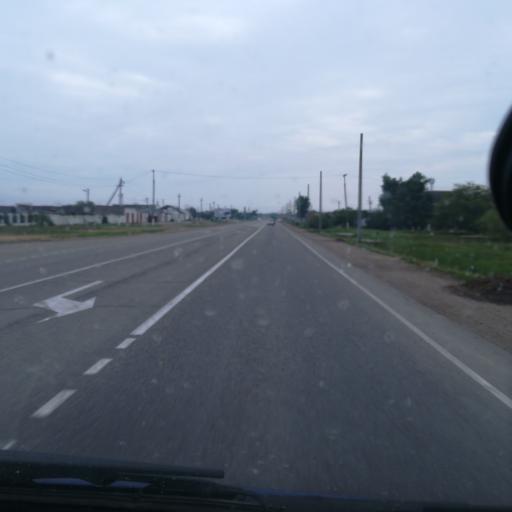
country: RU
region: Krasnodarskiy
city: Kiyevskoye
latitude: 44.9992
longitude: 37.9384
